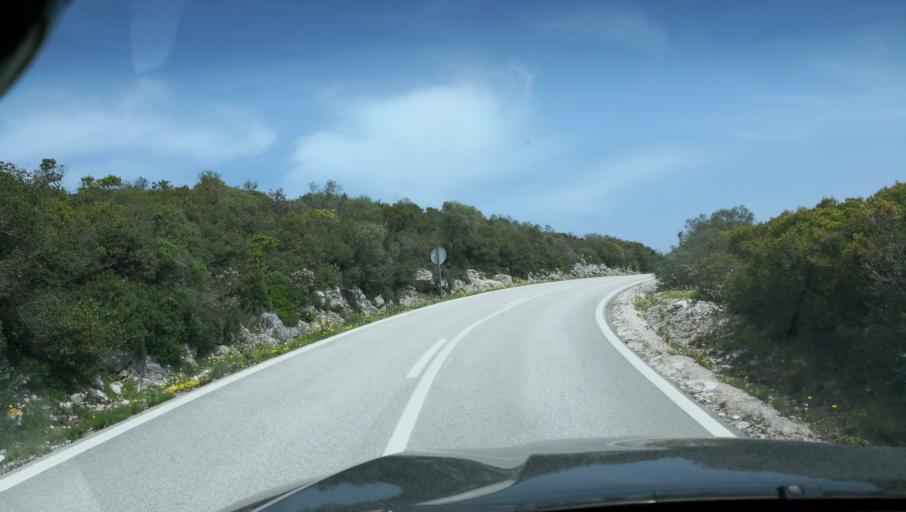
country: PT
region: Setubal
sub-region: Palmela
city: Quinta do Anjo
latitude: 38.4865
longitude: -8.9876
